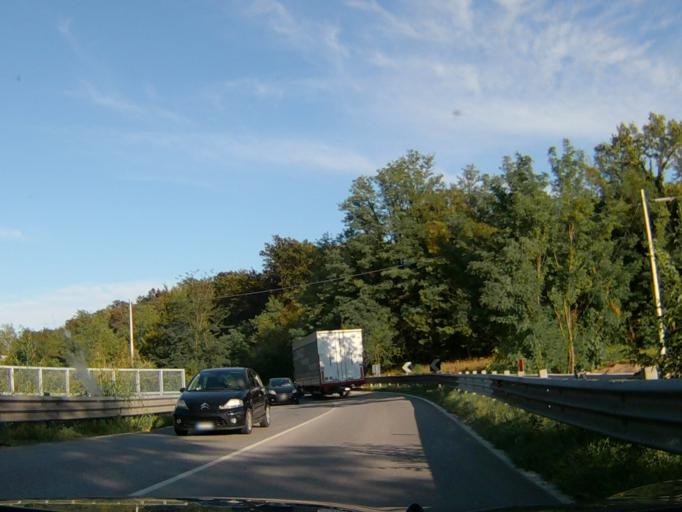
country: IT
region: Lombardy
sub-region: Provincia di Brescia
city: Lonato
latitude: 45.4621
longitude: 10.4995
